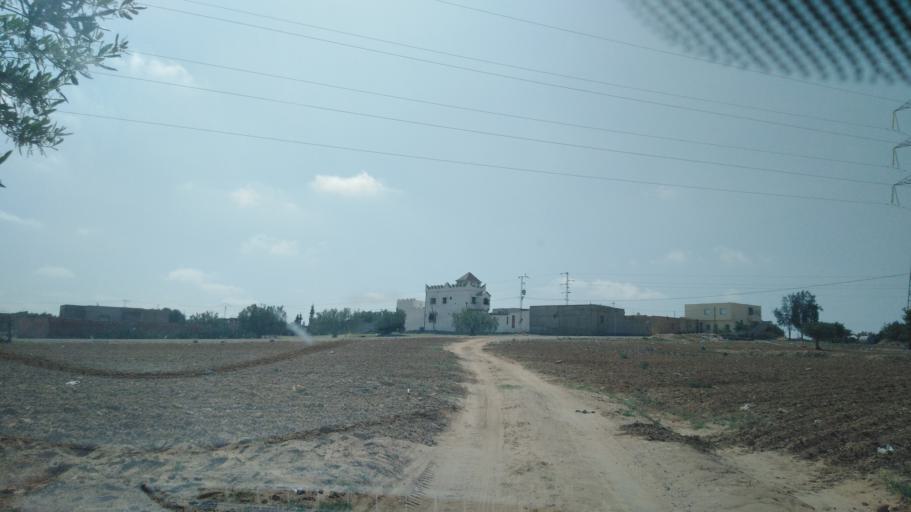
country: TN
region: Safaqis
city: Sfax
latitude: 34.7308
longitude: 10.5630
